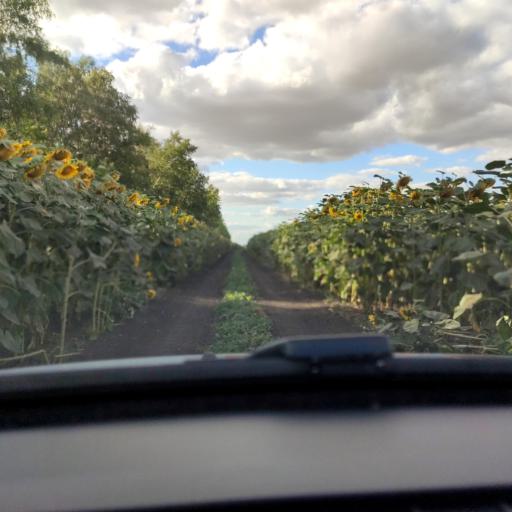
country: RU
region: Voronezj
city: Verkhnyaya Khava
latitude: 51.5998
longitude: 39.8401
